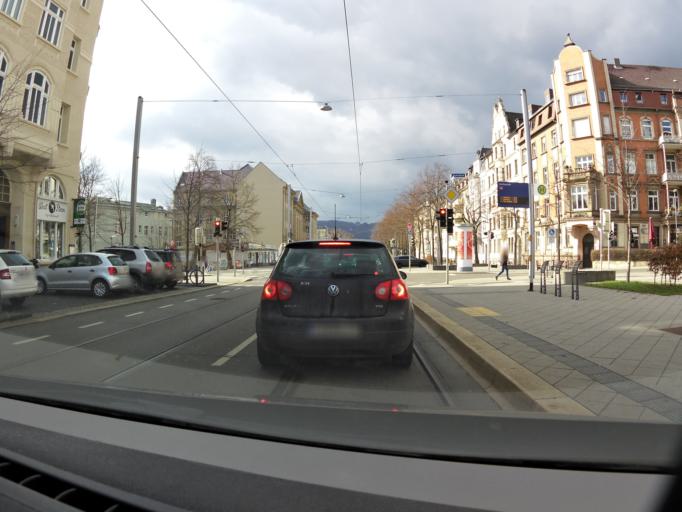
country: DE
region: Hesse
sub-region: Regierungsbezirk Kassel
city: Kassel
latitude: 51.3145
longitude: 9.4733
